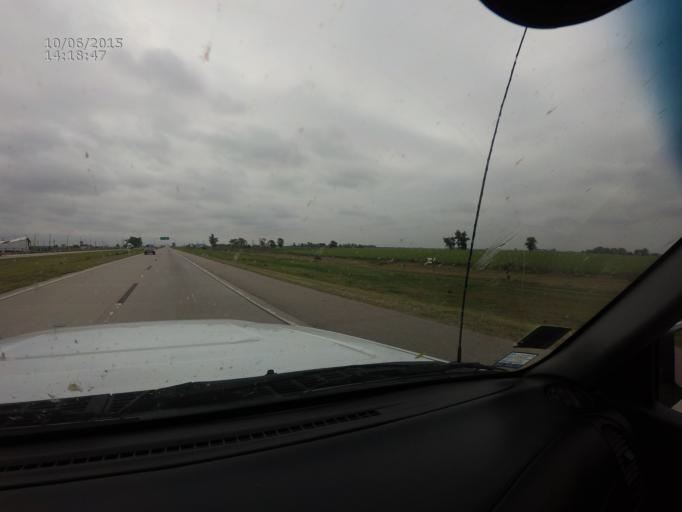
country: AR
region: Cordoba
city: Villa Maria
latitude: -32.3662
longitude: -63.2269
